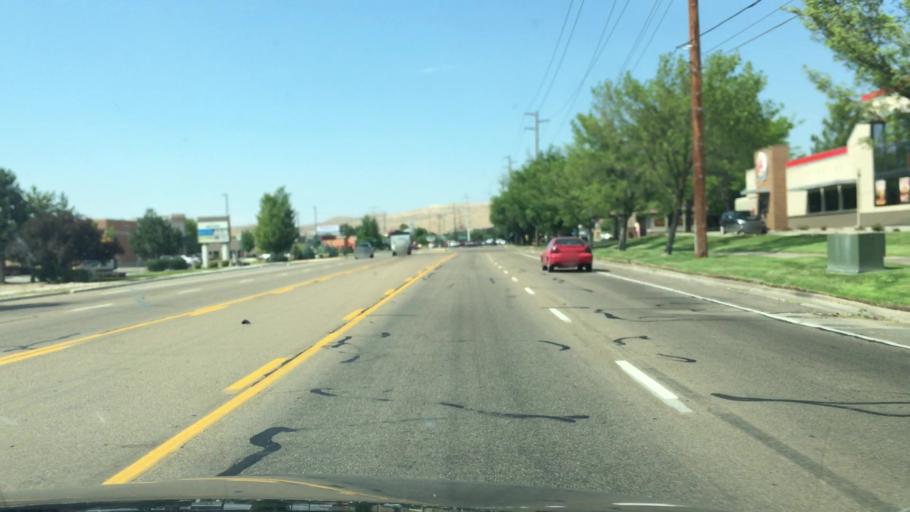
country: US
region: Idaho
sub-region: Ada County
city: Garden City
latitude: 43.6651
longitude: -116.2793
